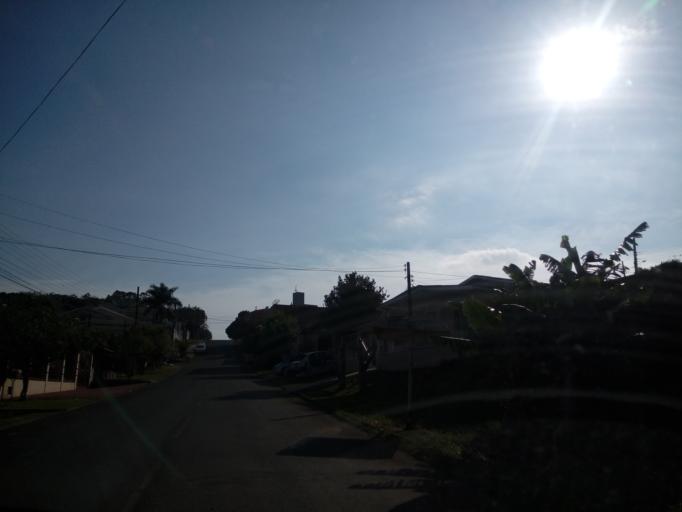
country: BR
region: Santa Catarina
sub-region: Chapeco
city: Chapeco
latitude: -27.1234
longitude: -52.6148
